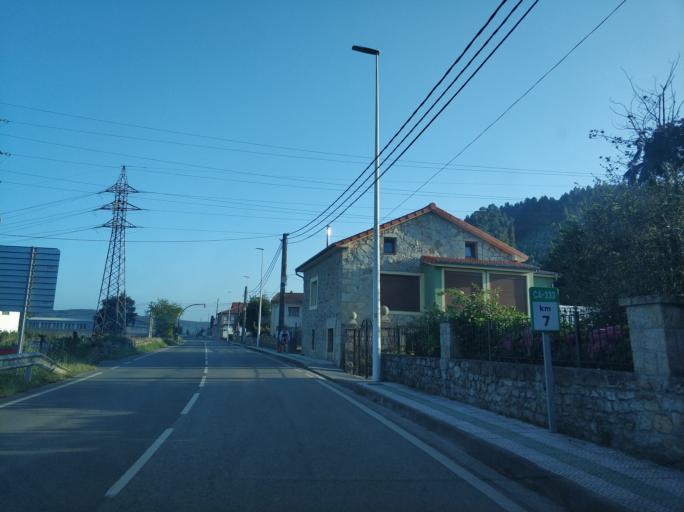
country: ES
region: Cantabria
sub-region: Provincia de Cantabria
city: Puente Viesgo
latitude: 43.3589
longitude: -3.9558
